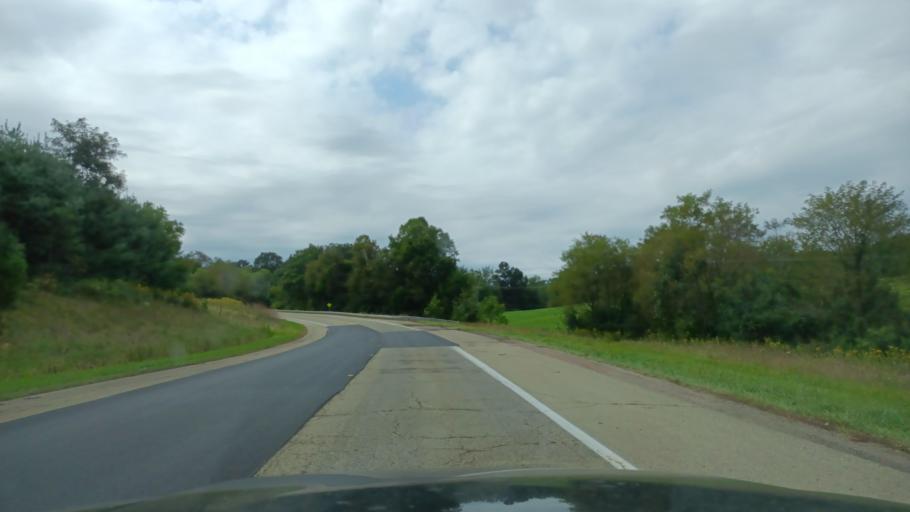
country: US
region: Ohio
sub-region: Vinton County
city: McArthur
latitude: 39.2793
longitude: -82.5332
